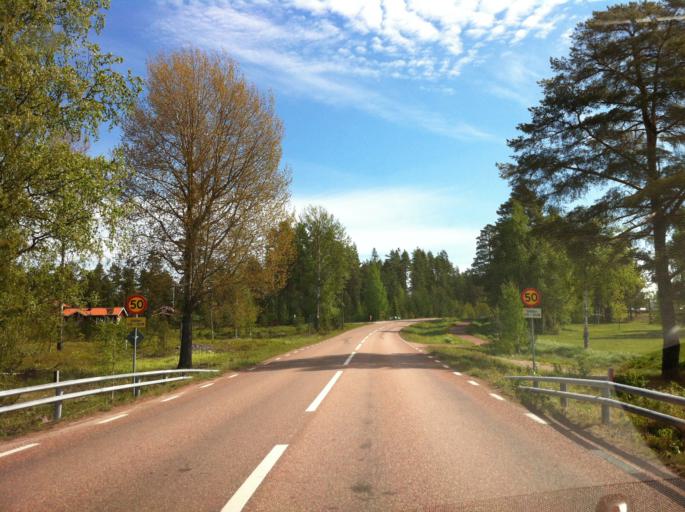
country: SE
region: Dalarna
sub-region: Mora Kommun
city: Mora
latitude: 60.9000
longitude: 14.5759
